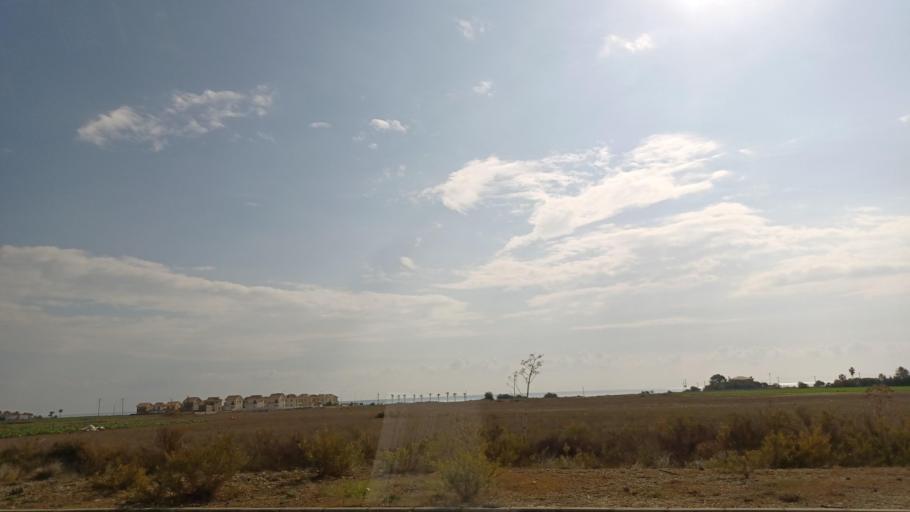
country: CY
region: Larnaka
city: Perivolia
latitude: 34.8251
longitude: 33.5543
